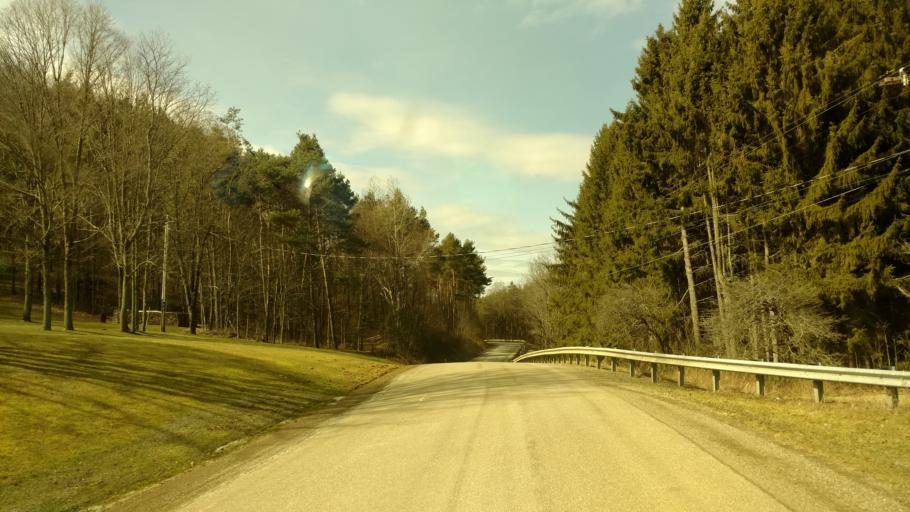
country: US
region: New York
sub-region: Allegany County
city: Wellsville
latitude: 41.9537
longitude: -77.8311
